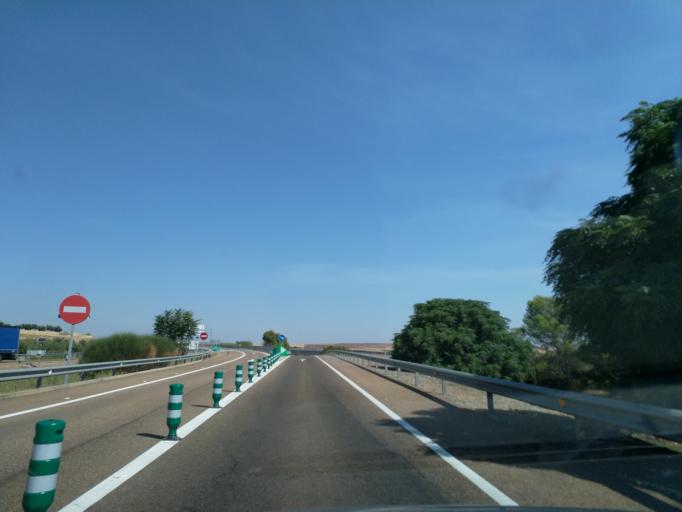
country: ES
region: Extremadura
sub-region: Provincia de Badajoz
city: Merida
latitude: 38.9446
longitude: -6.3419
